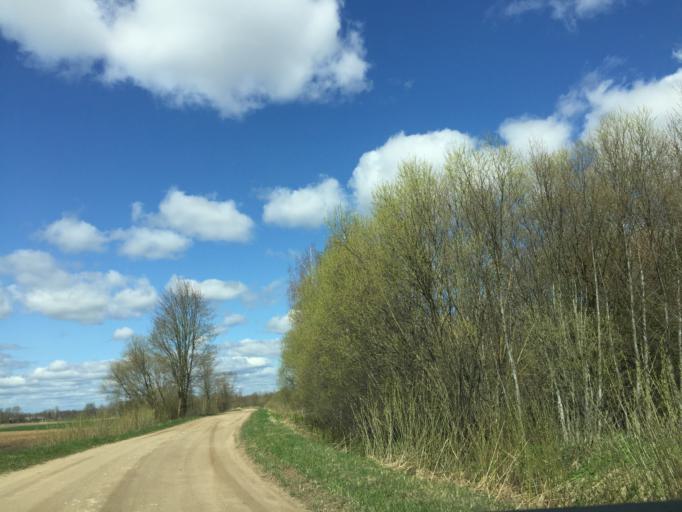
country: LV
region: Vilanu
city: Vilani
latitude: 56.6651
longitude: 27.1049
